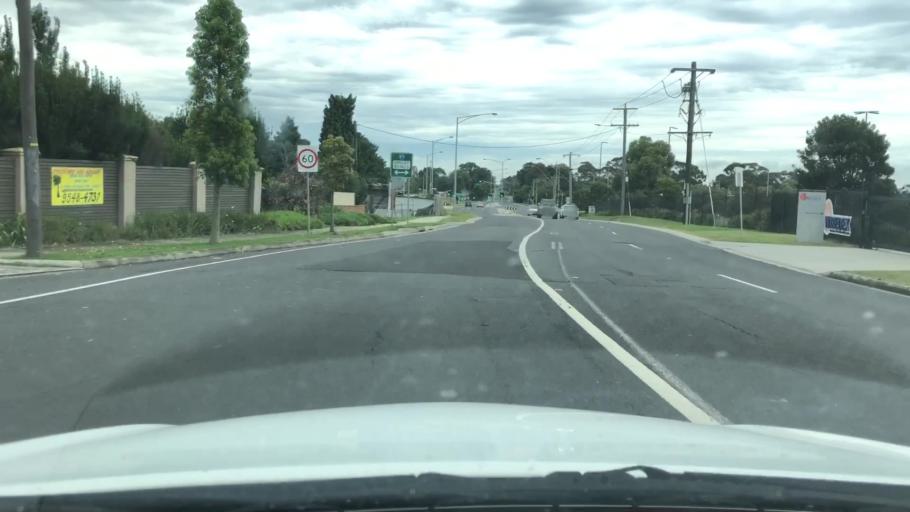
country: AU
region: Victoria
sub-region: Greater Dandenong
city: Springvale South
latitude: -37.9605
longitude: 145.1304
